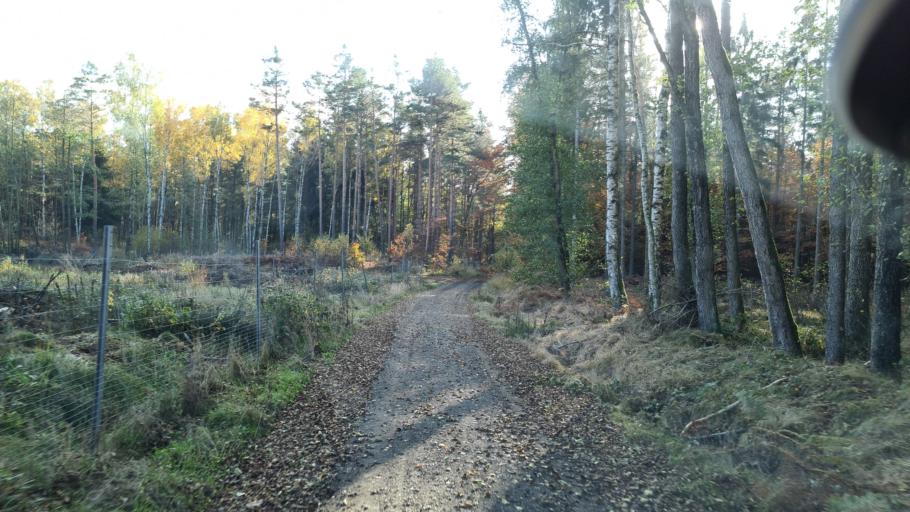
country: DE
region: Saxony
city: Dahlen
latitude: 51.4171
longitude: 13.0052
